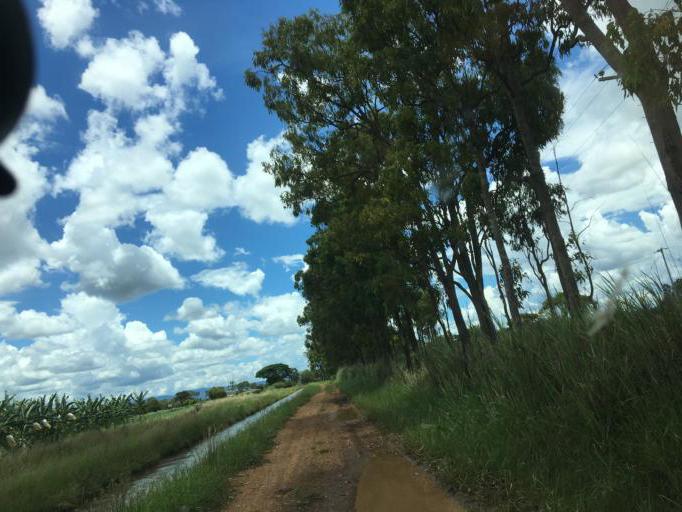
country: AU
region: Queensland
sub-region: Tablelands
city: Mareeba
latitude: -16.9891
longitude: 145.5252
